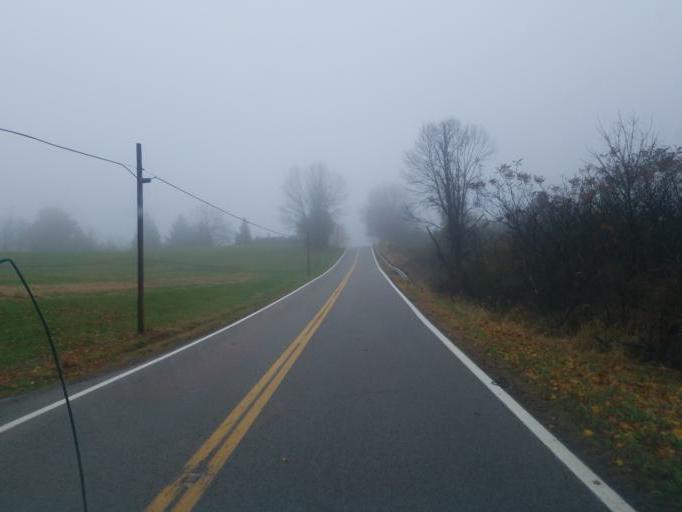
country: US
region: Ohio
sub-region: Morgan County
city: McConnelsville
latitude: 39.5964
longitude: -81.8650
